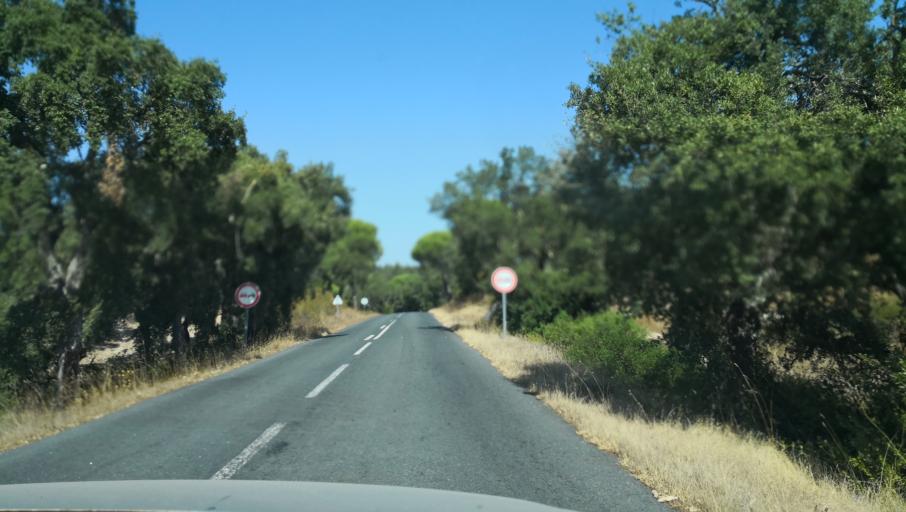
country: PT
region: Setubal
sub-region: Alcacer do Sal
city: Alcacer do Sal
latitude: 38.2990
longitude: -8.4044
